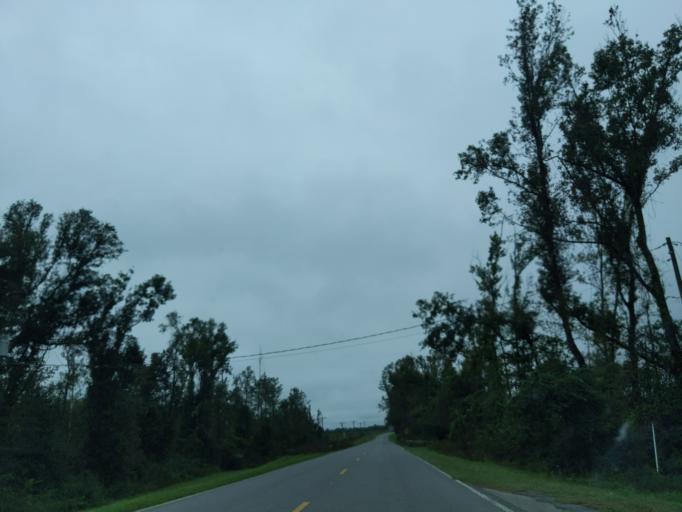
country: US
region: Florida
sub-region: Jackson County
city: Sneads
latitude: 30.6975
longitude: -84.9237
